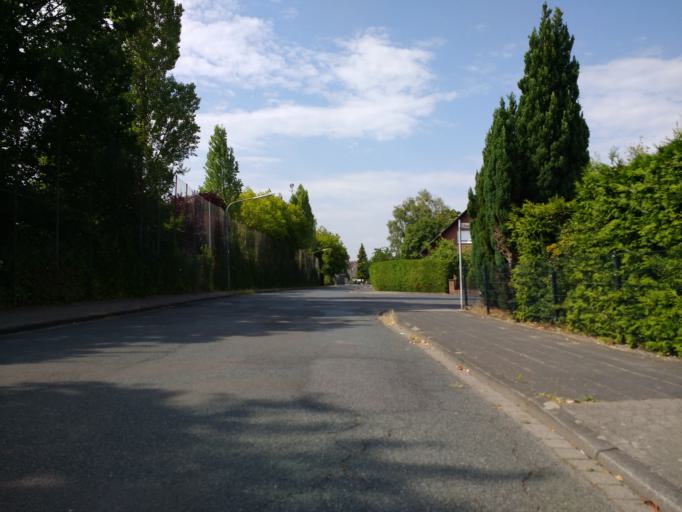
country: DE
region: Lower Saxony
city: Gifhorn
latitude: 52.4709
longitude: 10.5532
